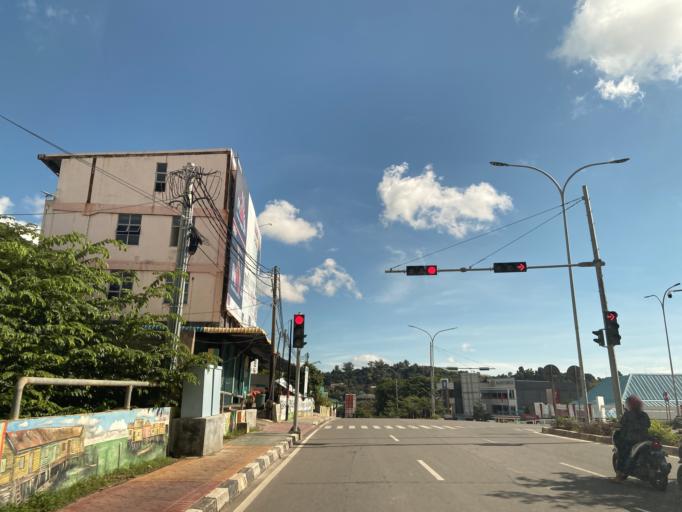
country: SG
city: Singapore
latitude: 1.1445
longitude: 104.0175
